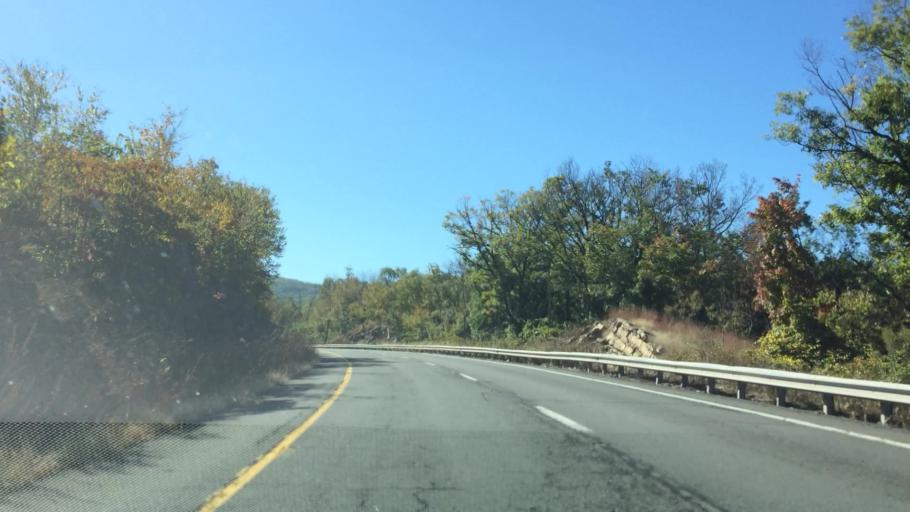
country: US
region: Pennsylvania
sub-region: Luzerne County
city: Ashley
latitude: 41.2044
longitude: -75.8970
